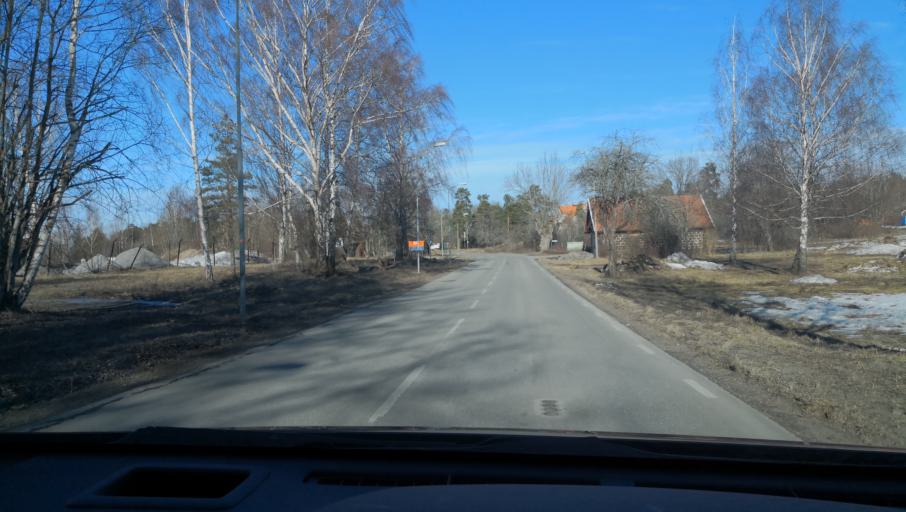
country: SE
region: Uppsala
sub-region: Osthammars Kommun
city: Osterbybruk
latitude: 60.2034
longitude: 17.8990
